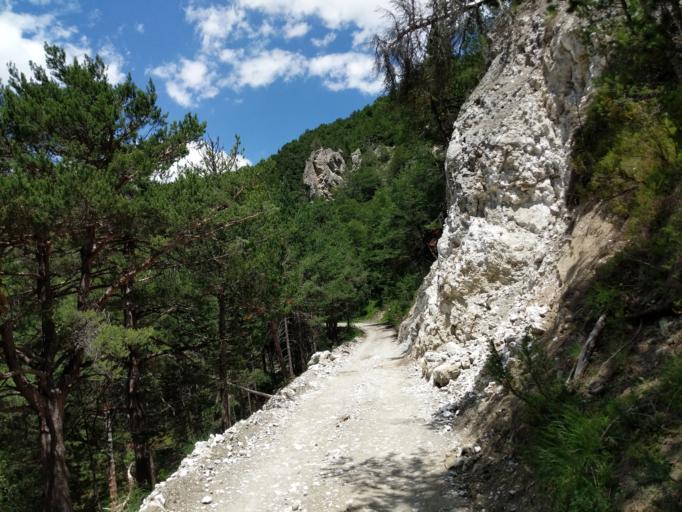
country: FR
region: Rhone-Alpes
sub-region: Departement de la Savoie
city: Modane
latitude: 45.2260
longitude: 6.7479
